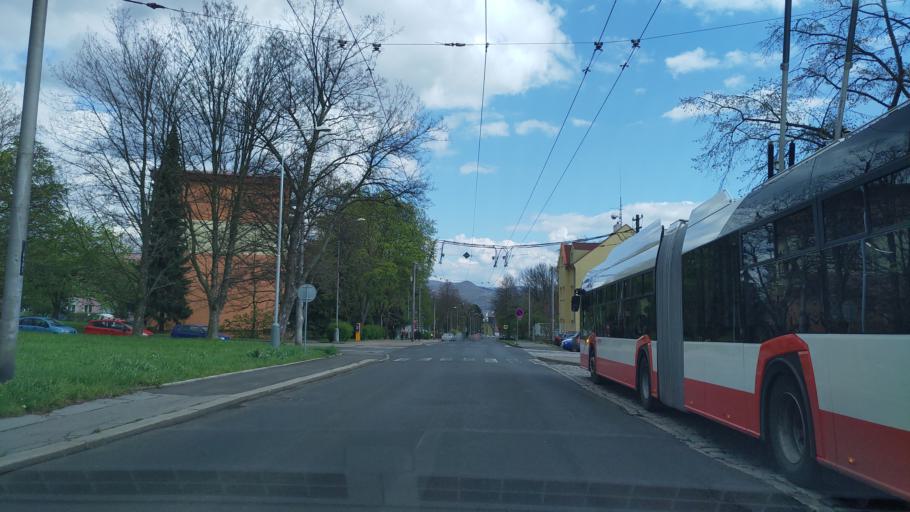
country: CZ
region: Ustecky
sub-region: Okres Usti nad Labem
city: Usti nad Labem
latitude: 50.6851
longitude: 13.9989
